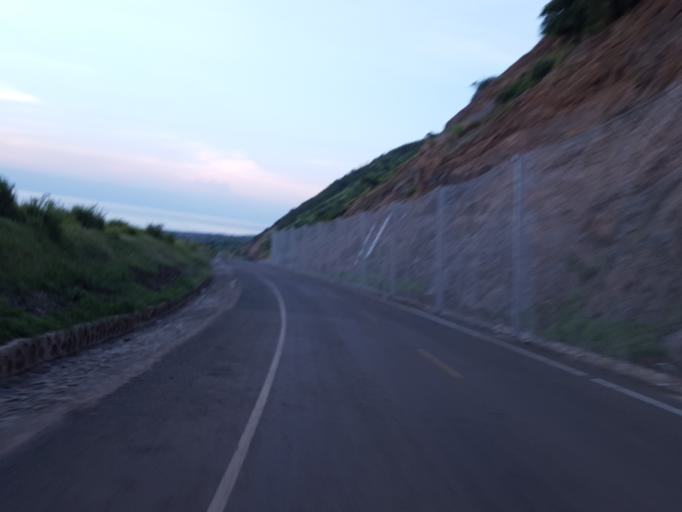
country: UG
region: Western Region
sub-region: Kibale District
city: Kagadi
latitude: 1.2441
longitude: 30.7585
